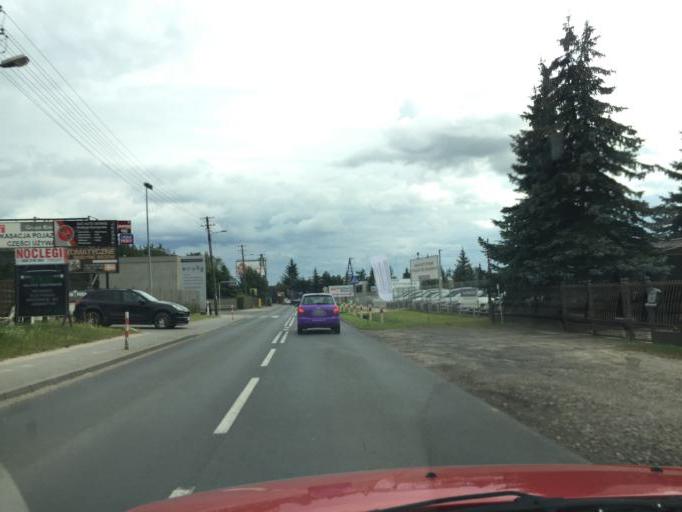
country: PL
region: Greater Poland Voivodeship
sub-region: Powiat poznanski
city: Baranowo
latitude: 52.4036
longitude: 16.7965
